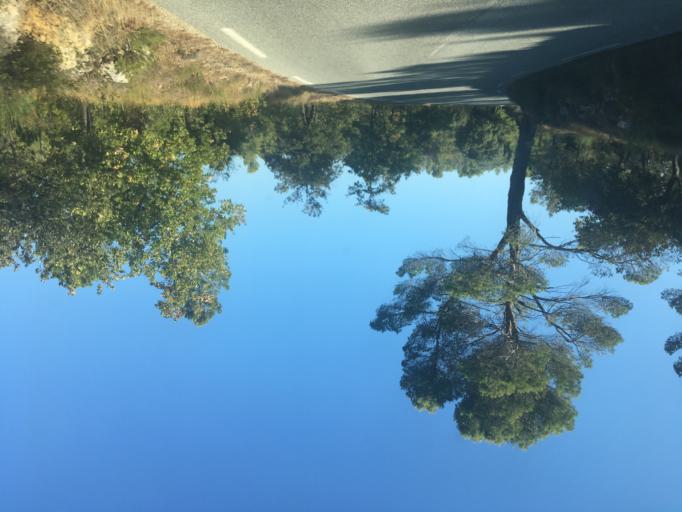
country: FR
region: Provence-Alpes-Cote d'Azur
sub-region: Departement du Var
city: Salernes
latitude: 43.5887
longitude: 6.2254
